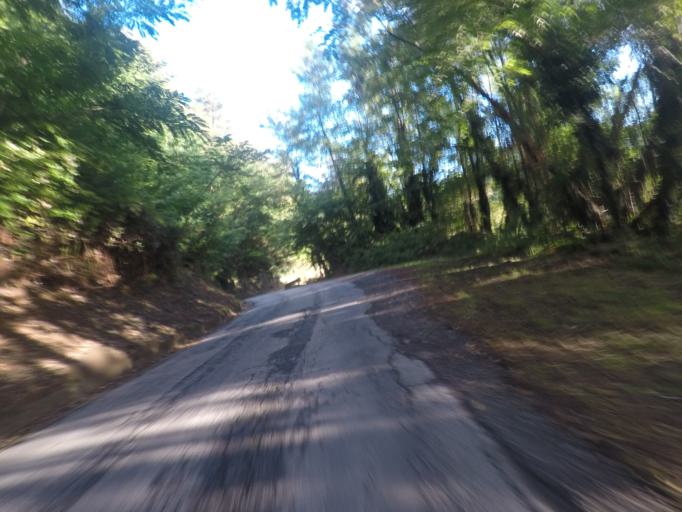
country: IT
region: Tuscany
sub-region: Provincia di Lucca
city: Massarosa
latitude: 43.9118
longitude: 10.3687
